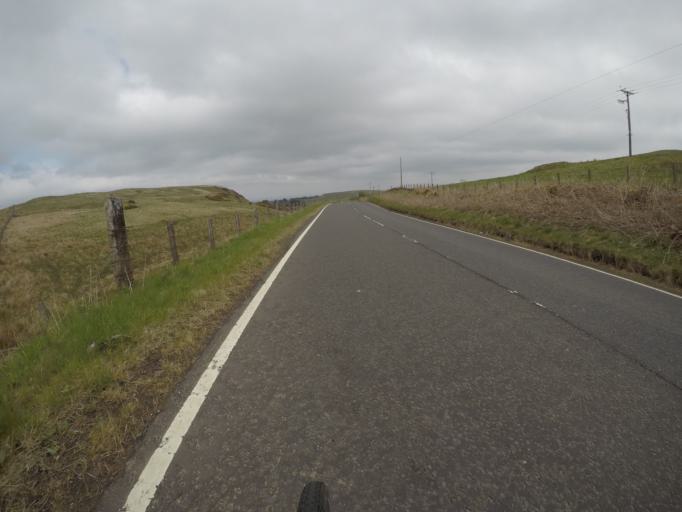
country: GB
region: Scotland
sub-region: East Renfrewshire
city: Neilston
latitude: 55.7442
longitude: -4.4021
